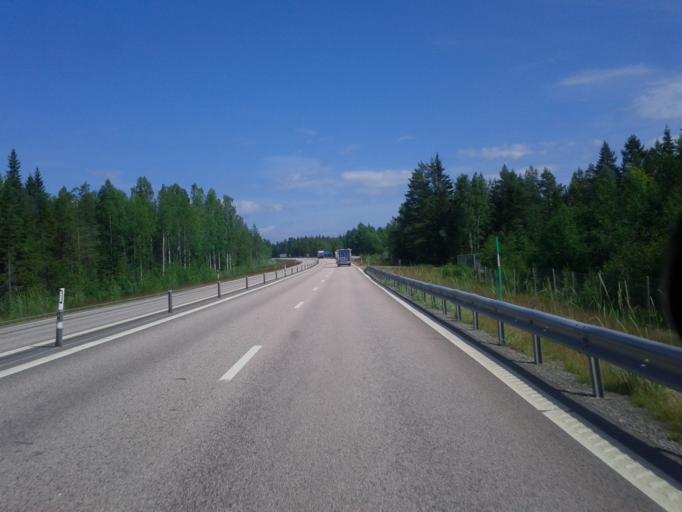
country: SE
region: Vaesternorrland
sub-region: OErnskoeldsviks Kommun
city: Husum
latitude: 63.4703
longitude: 19.2791
